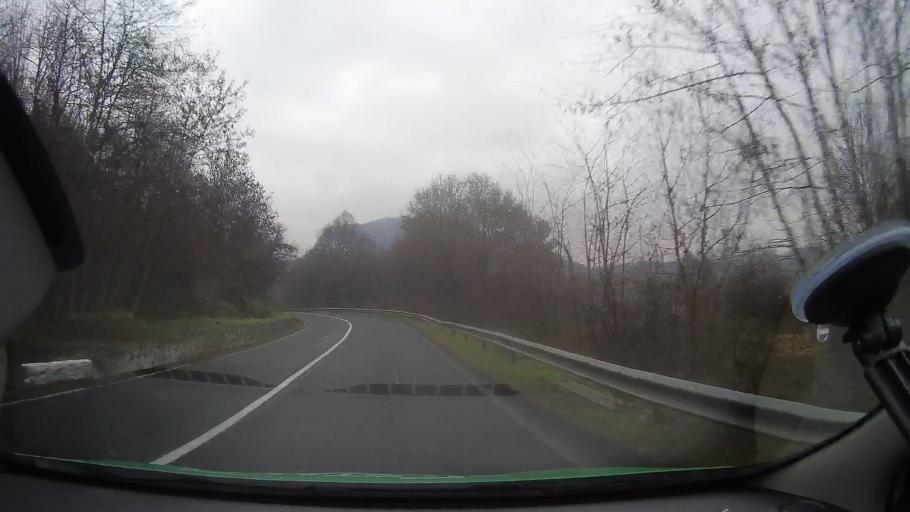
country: RO
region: Arad
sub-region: Comuna Plescuta
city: Plescuta
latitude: 46.2951
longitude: 22.4399
